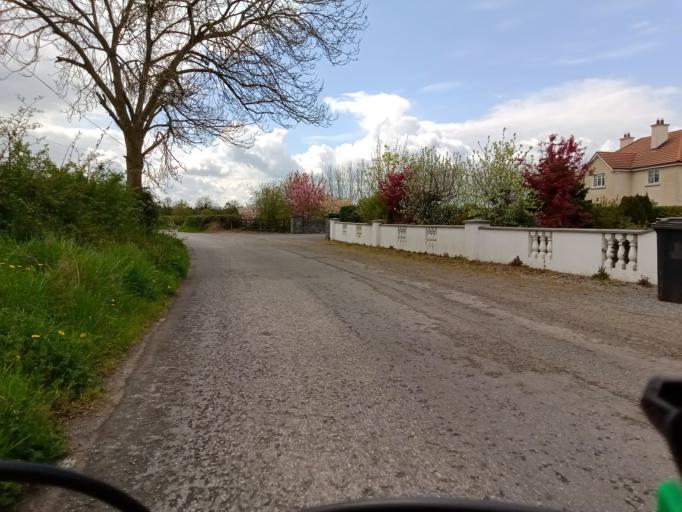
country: IE
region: Leinster
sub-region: Kilkenny
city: Kilkenny
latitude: 52.6359
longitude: -7.2789
